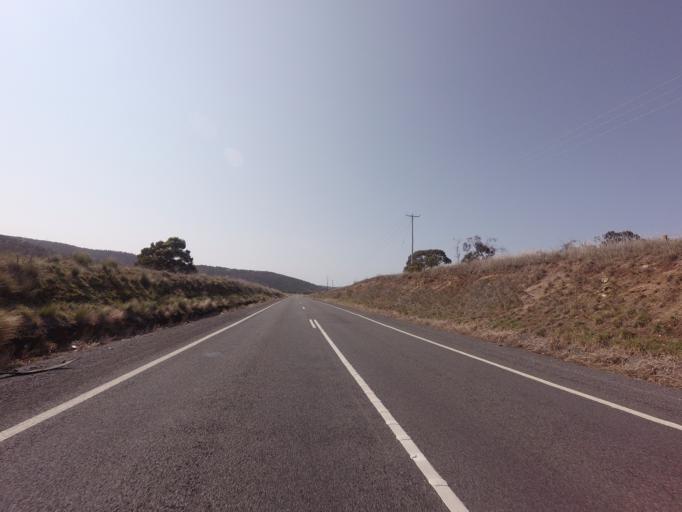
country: AU
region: Tasmania
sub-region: Northern Midlands
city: Evandale
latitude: -41.8137
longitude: 147.5822
